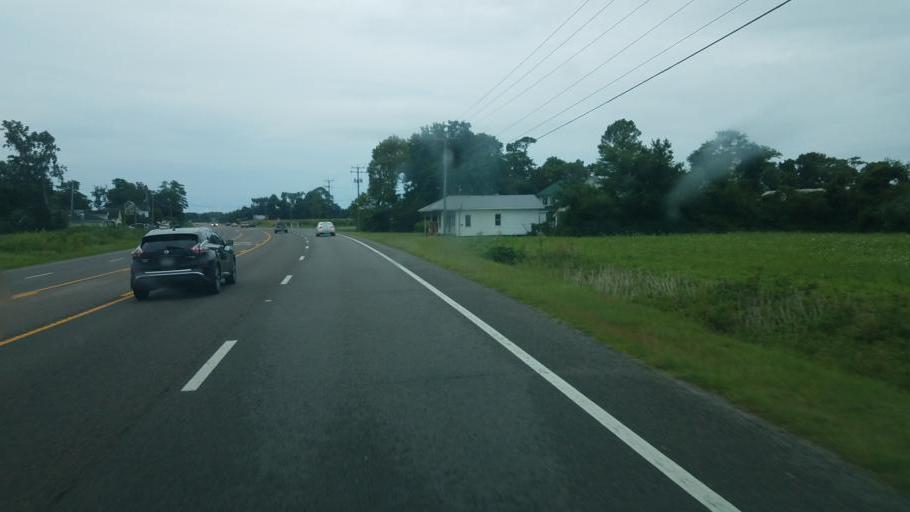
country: US
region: North Carolina
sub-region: Dare County
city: Southern Shores
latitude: 36.2044
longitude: -75.8656
